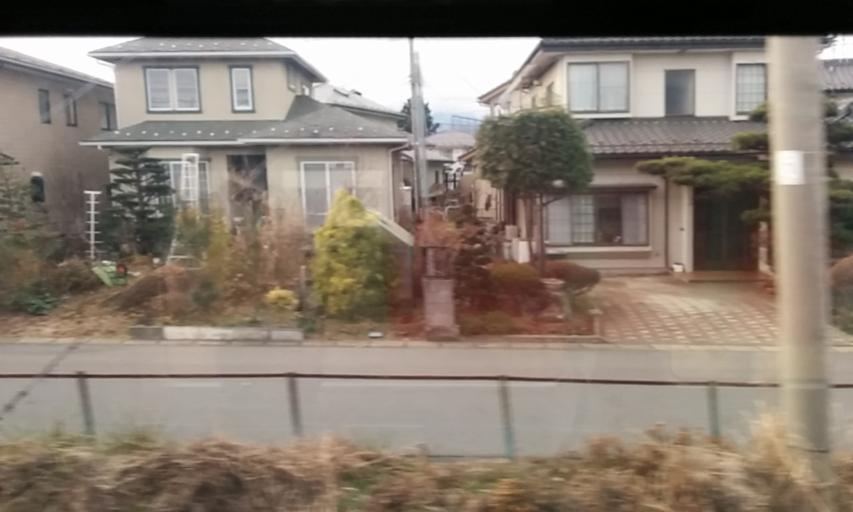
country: JP
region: Nagano
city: Shiojiri
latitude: 36.1207
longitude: 137.9480
